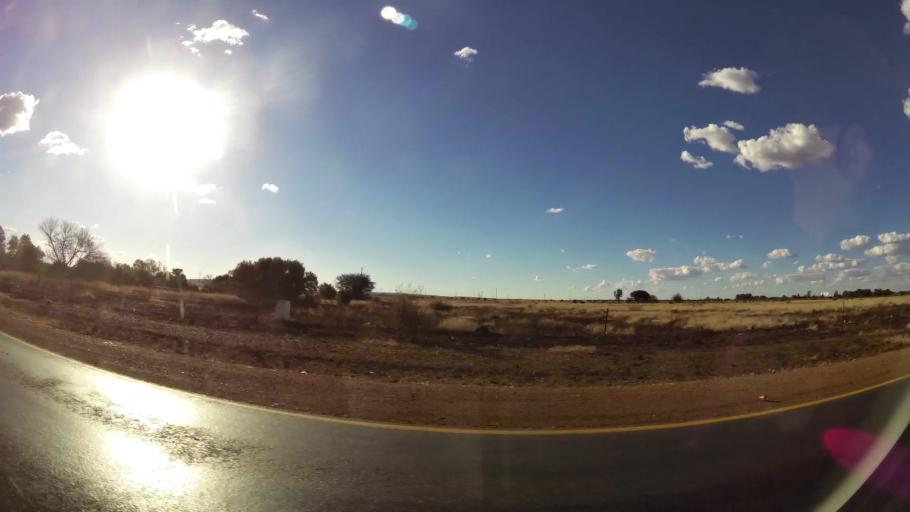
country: ZA
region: North-West
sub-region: Dr Kenneth Kaunda District Municipality
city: Stilfontein
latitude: -26.8424
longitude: 26.7442
